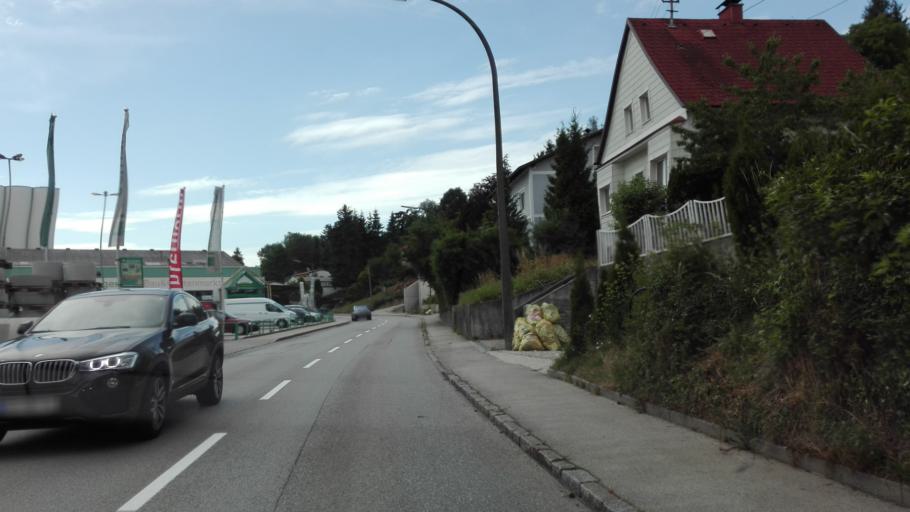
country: AT
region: Upper Austria
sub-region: Politischer Bezirk Grieskirchen
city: Grieskirchen
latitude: 48.2307
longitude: 13.8429
